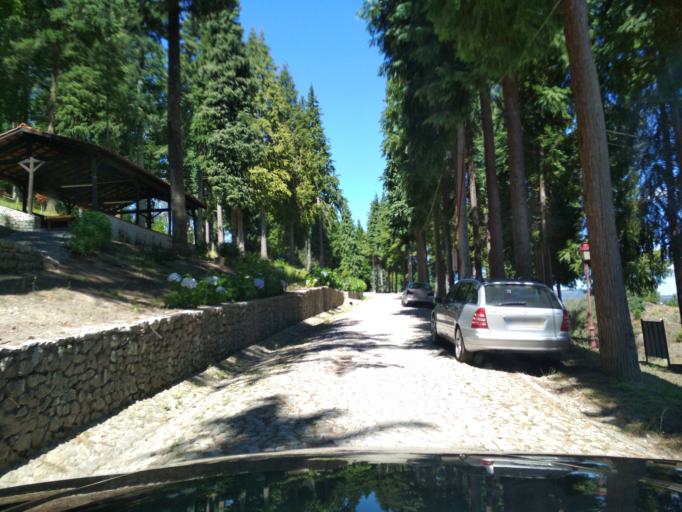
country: PT
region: Vila Real
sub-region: Ribeira de Pena
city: Ribeira de Pena
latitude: 41.5150
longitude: -7.8012
